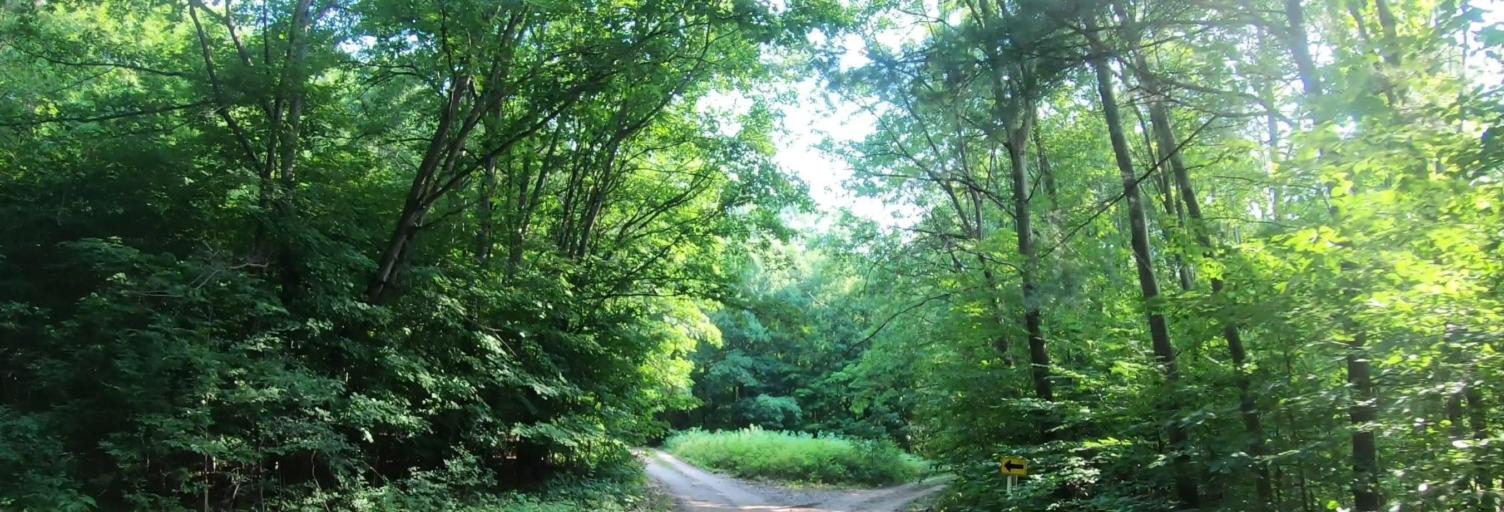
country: US
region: Michigan
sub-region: Benzie County
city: Beulah
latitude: 44.7702
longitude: -85.9269
